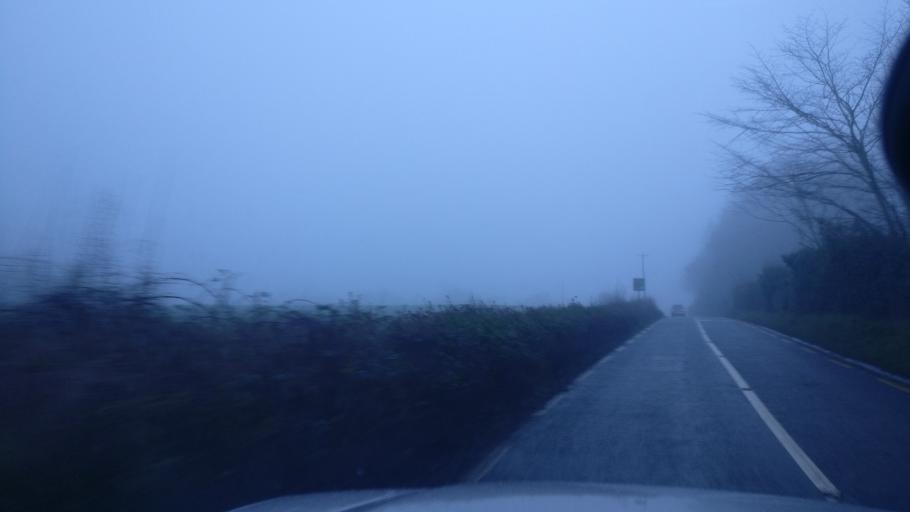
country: IE
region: Connaught
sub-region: County Galway
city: Portumna
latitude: 53.0890
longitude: -8.1832
